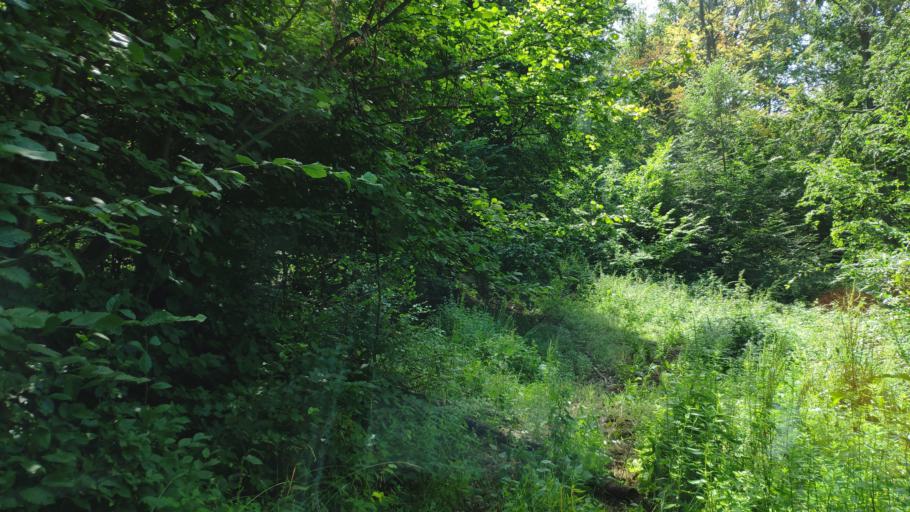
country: SK
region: Kosicky
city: Dobsina
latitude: 48.7125
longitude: 20.3858
